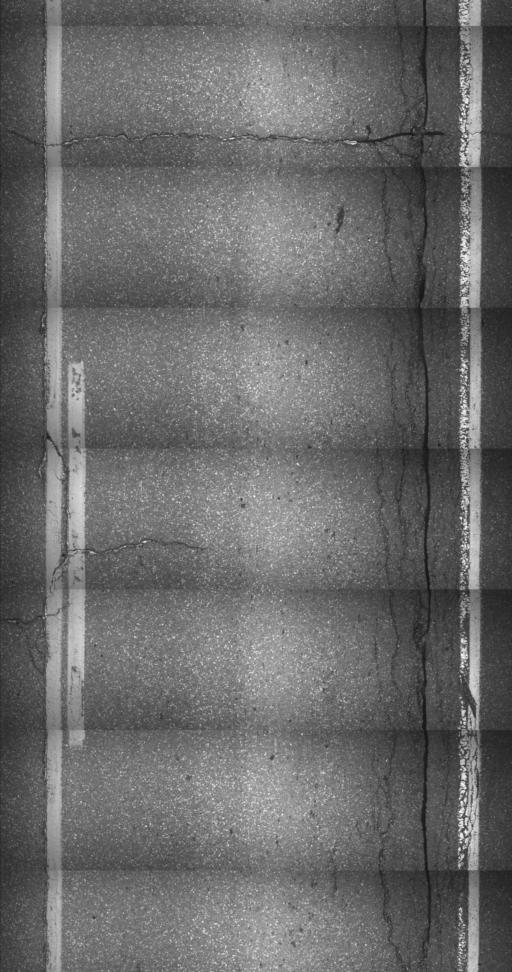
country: US
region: Vermont
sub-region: Orleans County
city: Newport
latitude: 44.8471
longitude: -72.2623
